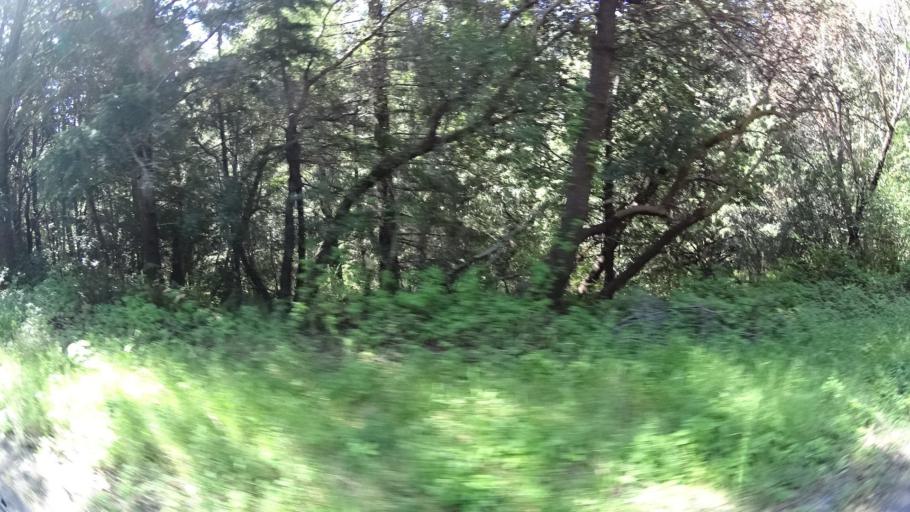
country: US
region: California
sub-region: Humboldt County
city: Rio Dell
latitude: 40.2700
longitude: -124.2196
